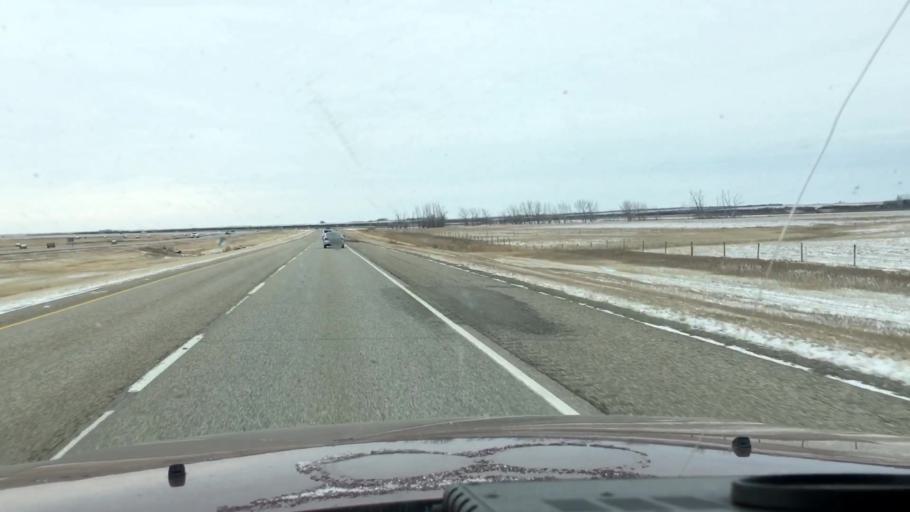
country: CA
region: Saskatchewan
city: Saskatoon
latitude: 51.4815
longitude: -106.2504
